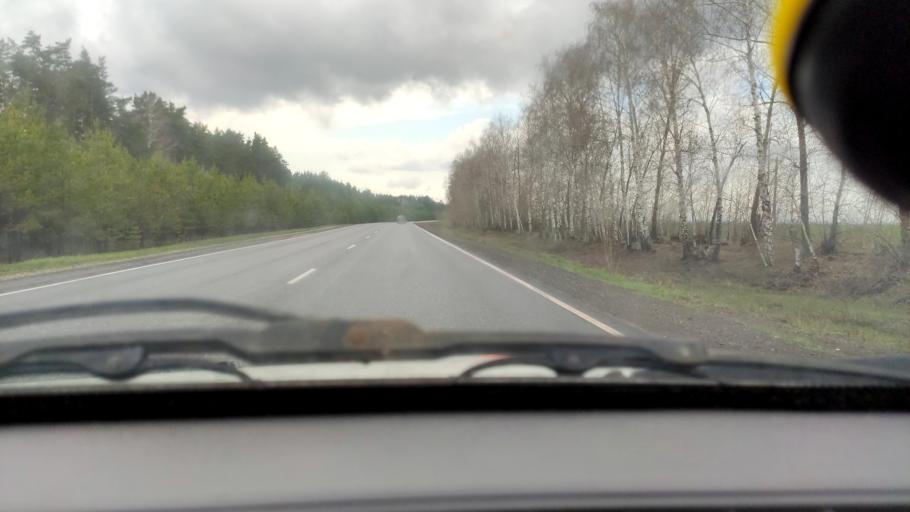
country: RU
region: Samara
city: Povolzhskiy
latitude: 53.6270
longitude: 49.6537
